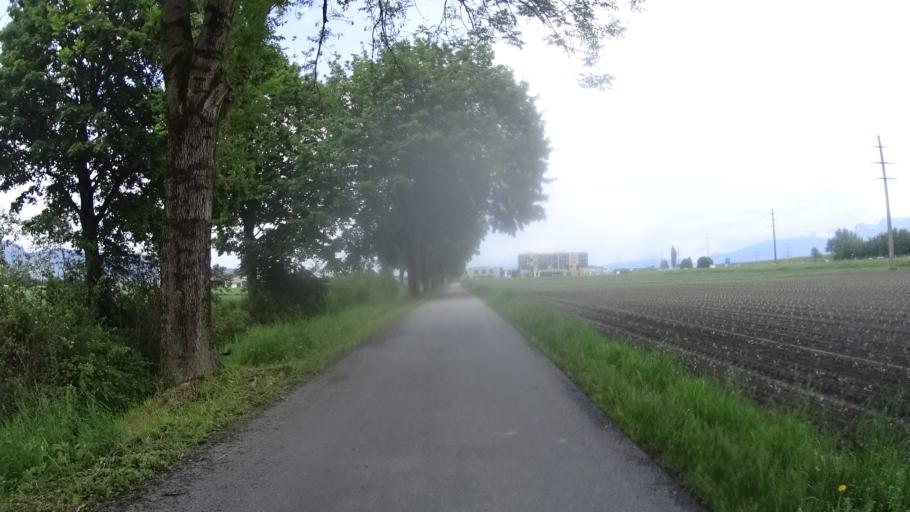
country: AT
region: Vorarlberg
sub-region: Politischer Bezirk Feldkirch
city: Mader
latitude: 47.3551
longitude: 9.6029
